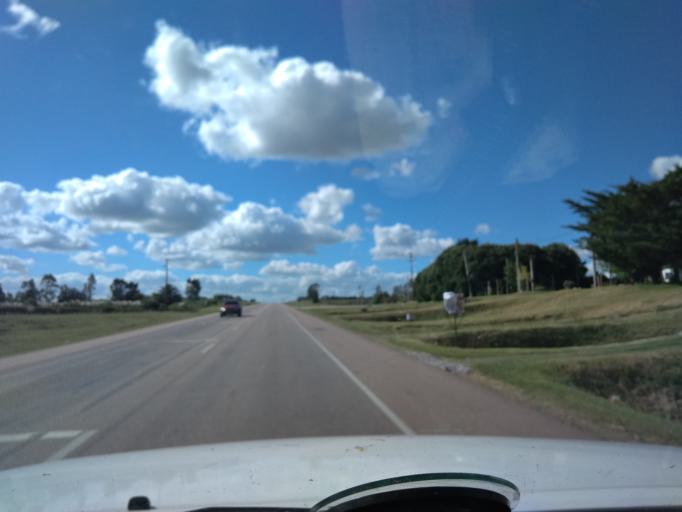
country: UY
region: Canelones
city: Canelones
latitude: -34.4935
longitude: -56.2819
